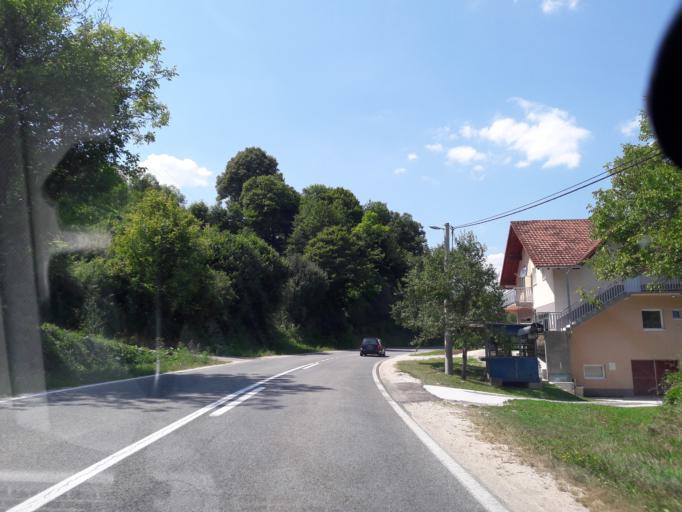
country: BA
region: Republika Srpska
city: Mrkonjic Grad
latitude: 44.3679
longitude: 17.1470
